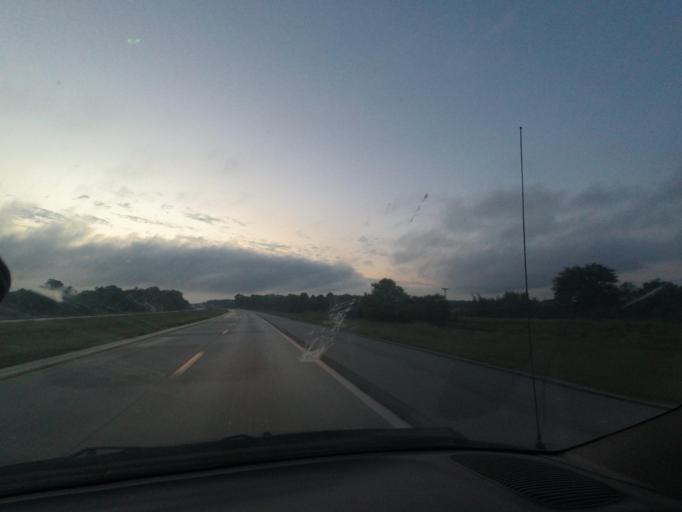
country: US
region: Missouri
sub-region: Linn County
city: Brookfield
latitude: 39.7646
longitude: -93.0433
